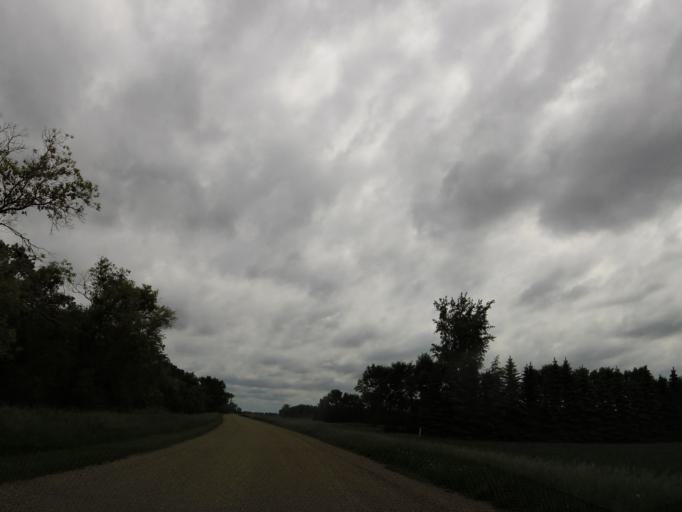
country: US
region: North Dakota
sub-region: Walsh County
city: Grafton
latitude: 48.4471
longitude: -97.4921
